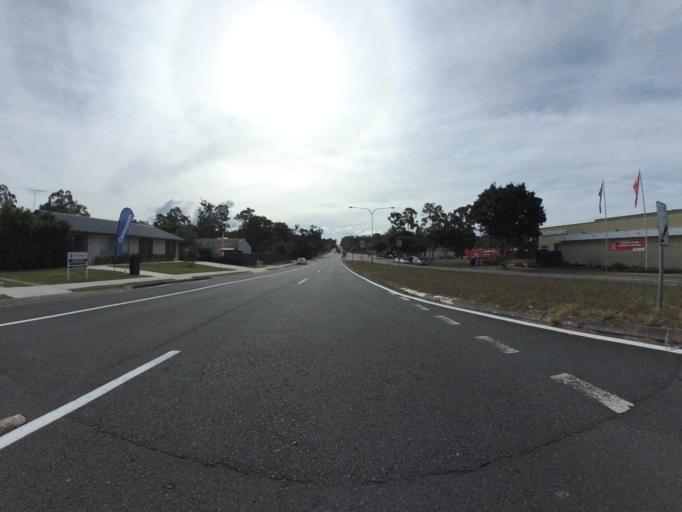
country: AU
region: Queensland
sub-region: Brisbane
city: Riverhills
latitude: -27.5640
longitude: 152.8864
